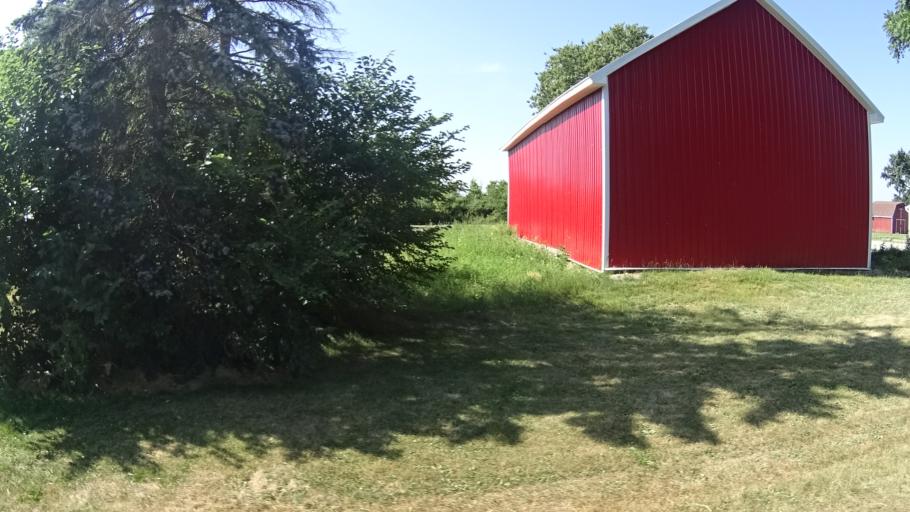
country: US
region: Ohio
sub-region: Huron County
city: Bellevue
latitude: 41.3747
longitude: -82.8141
